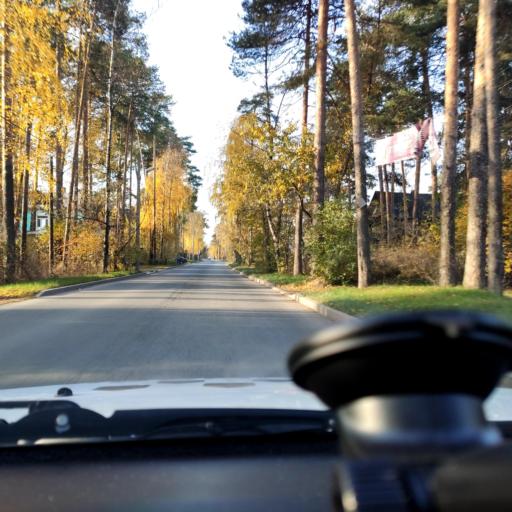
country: RU
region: Perm
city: Perm
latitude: 58.0511
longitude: 56.2912
